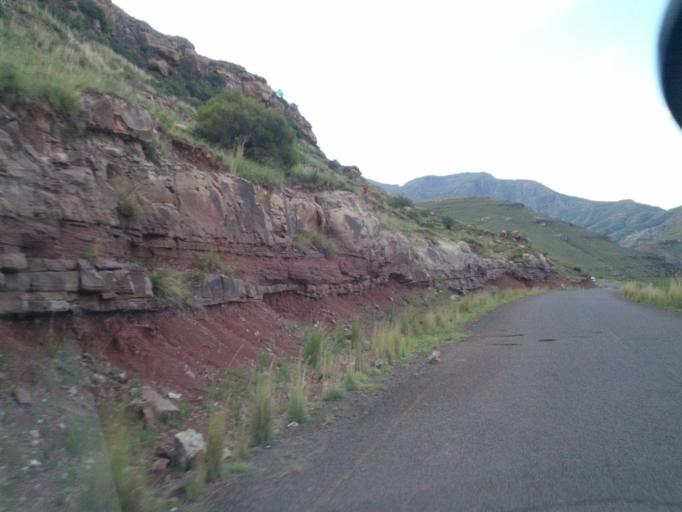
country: LS
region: Qacha's Nek
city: Qacha's Nek
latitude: -30.0575
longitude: 28.5031
